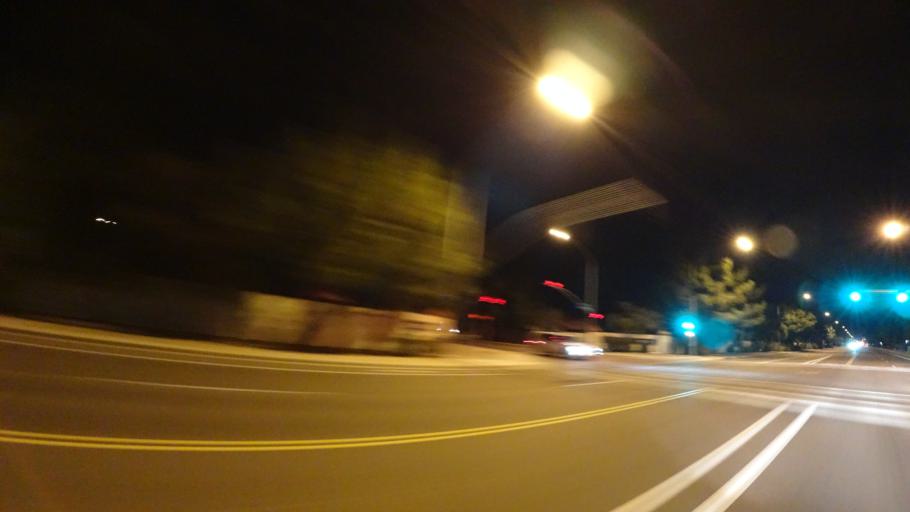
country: US
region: Arizona
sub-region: Maricopa County
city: Gilbert
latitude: 33.3937
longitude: -111.7480
